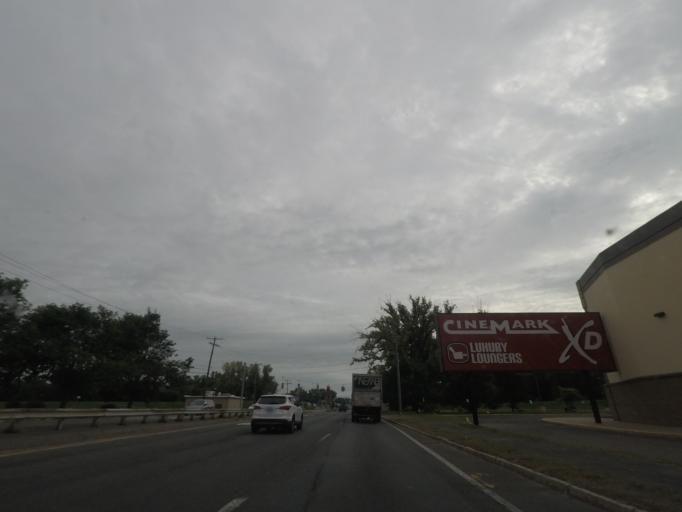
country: US
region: Massachusetts
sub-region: Hampden County
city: West Springfield
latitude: 42.1275
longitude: -72.6267
